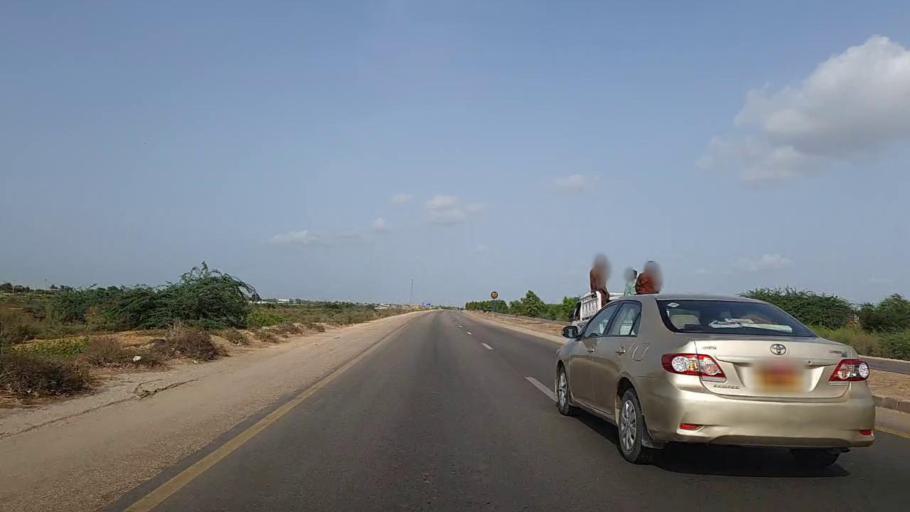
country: PK
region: Sindh
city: Gharo
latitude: 24.7394
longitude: 67.7410
